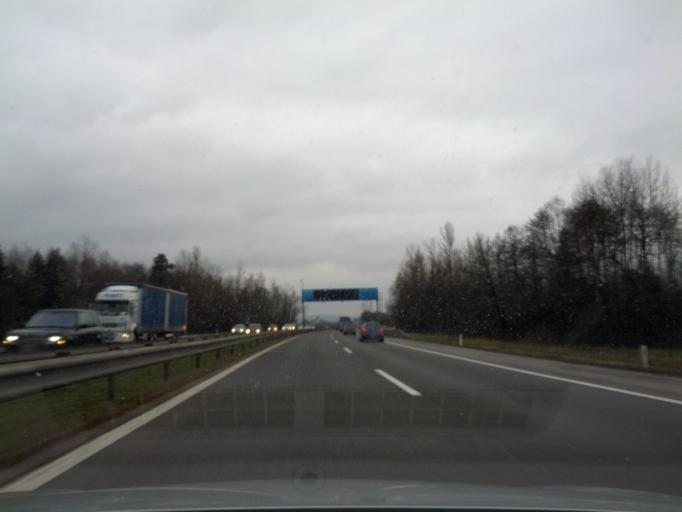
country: SI
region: Medvode
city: Zgornje Pirnice
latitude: 46.1336
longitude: 14.4803
